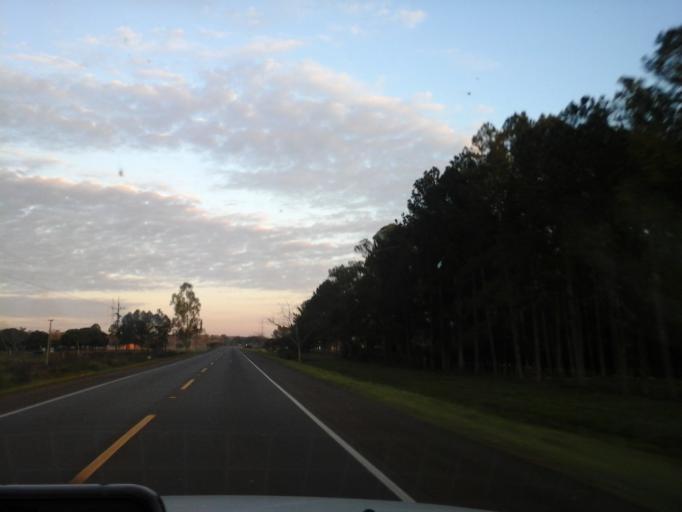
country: PY
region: Itapua
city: General Delgado
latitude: -27.0734
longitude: -56.5975
